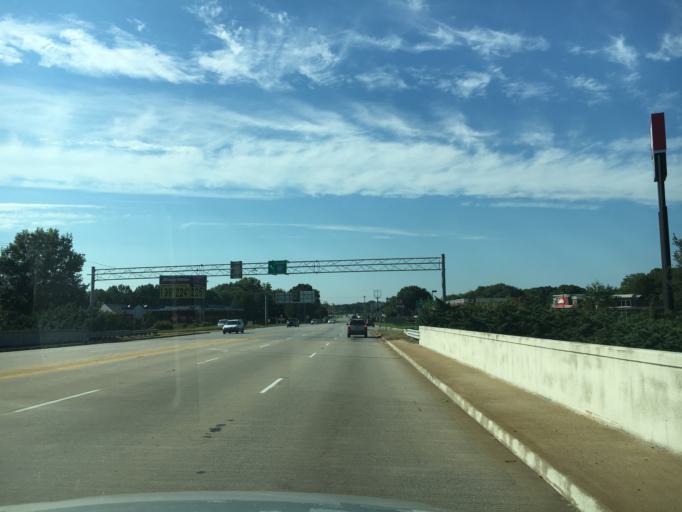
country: US
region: South Carolina
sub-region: Spartanburg County
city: Valley Falls
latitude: 35.0127
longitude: -81.9579
